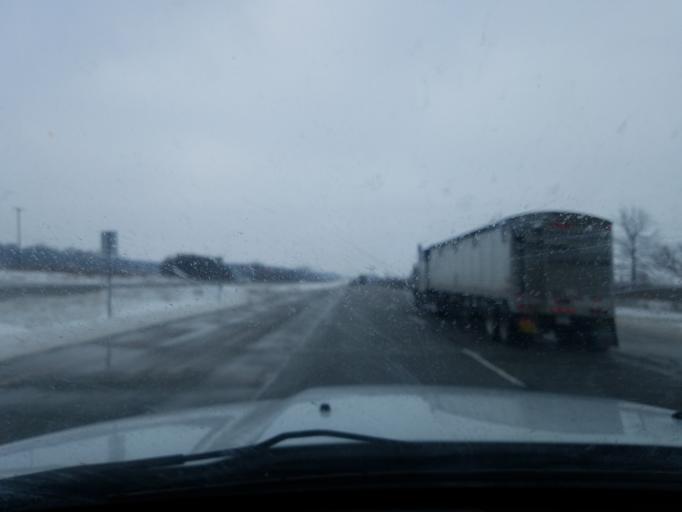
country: US
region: Indiana
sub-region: Marshall County
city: Argos
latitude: 41.1820
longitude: -86.2467
